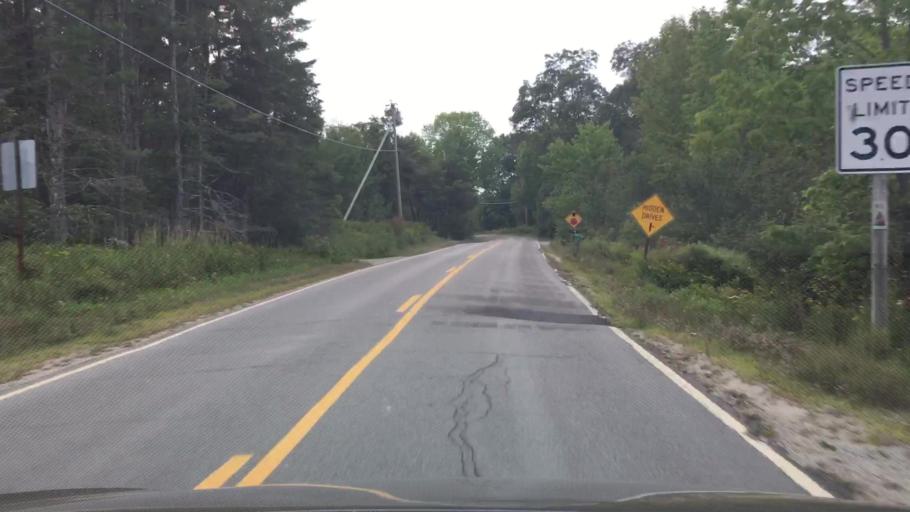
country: US
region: Maine
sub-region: Hancock County
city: Penobscot
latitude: 44.4514
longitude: -68.6988
